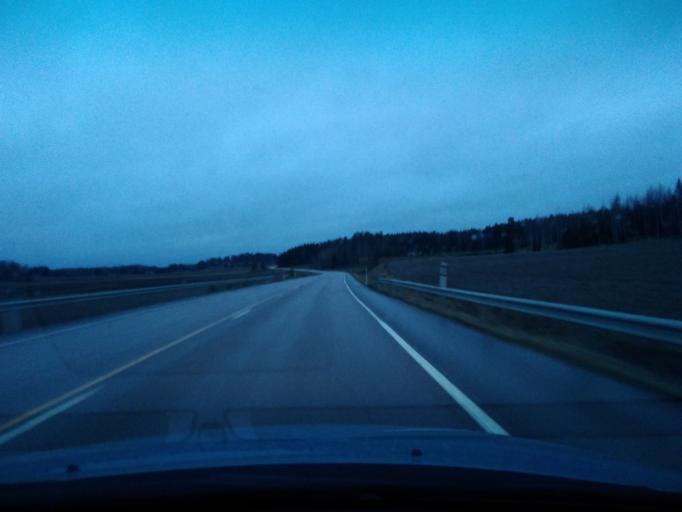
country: FI
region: Uusimaa
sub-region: Porvoo
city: Askola
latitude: 60.4795
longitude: 25.5645
